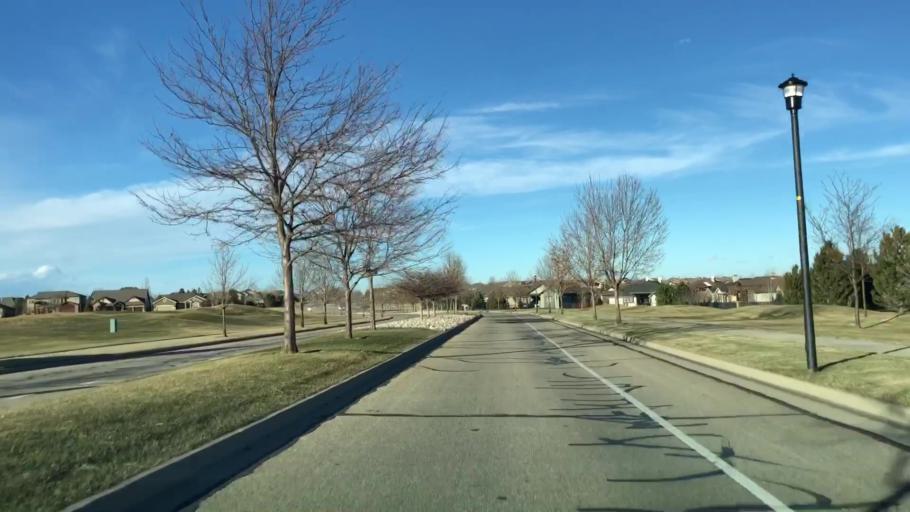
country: US
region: Colorado
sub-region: Weld County
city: Windsor
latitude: 40.4586
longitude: -104.9765
